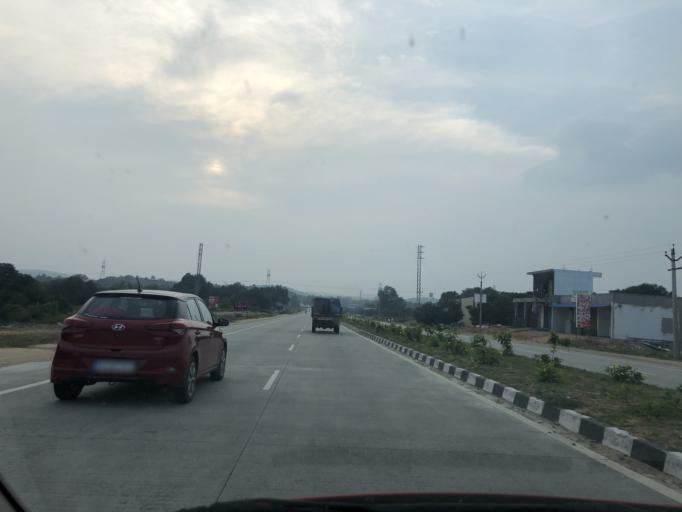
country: IN
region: Andhra Pradesh
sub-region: Chittoor
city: Chittoor
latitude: 13.1973
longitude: 78.9964
